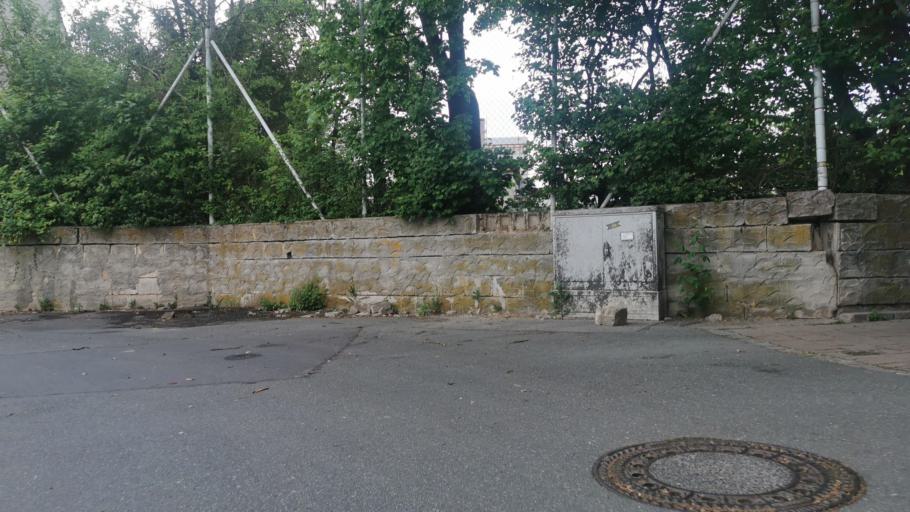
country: DE
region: Bavaria
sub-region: Regierungsbezirk Mittelfranken
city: Hochstadt an der Aisch
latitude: 49.7095
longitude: 10.8089
